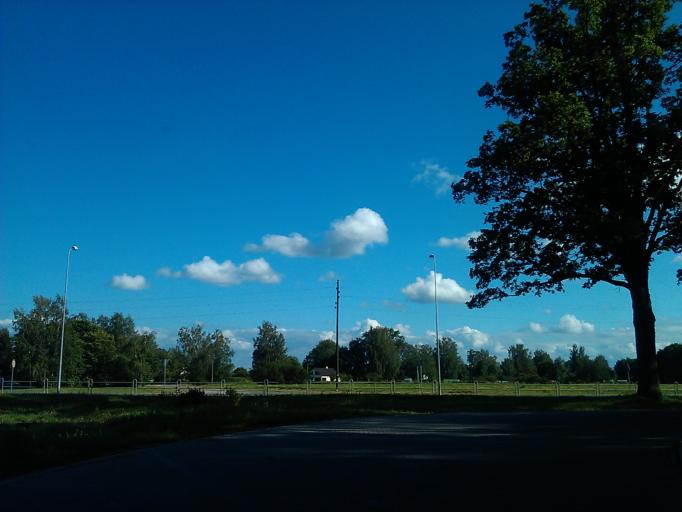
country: LV
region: Valmieras Rajons
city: Valmiera
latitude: 57.5557
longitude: 25.4345
